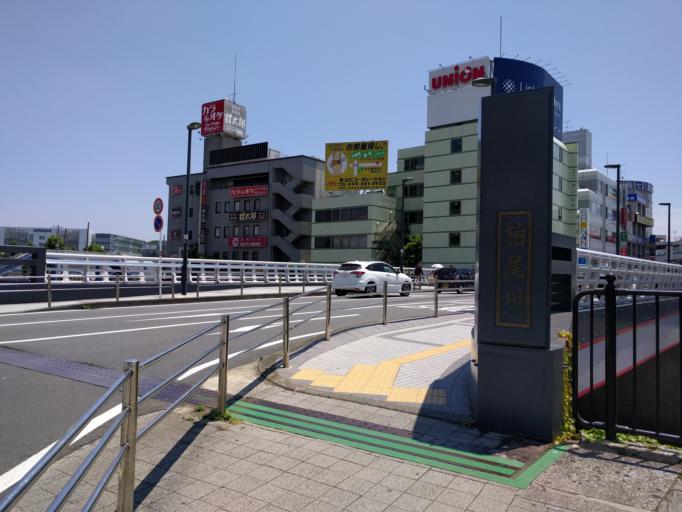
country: JP
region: Kanagawa
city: Fujisawa
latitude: 35.4006
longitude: 139.5352
